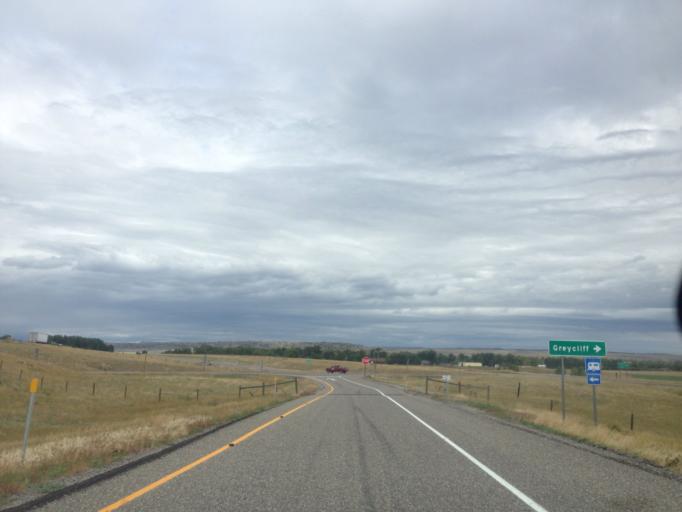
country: US
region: Montana
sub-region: Sweet Grass County
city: Big Timber
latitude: 45.7684
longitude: -109.7921
